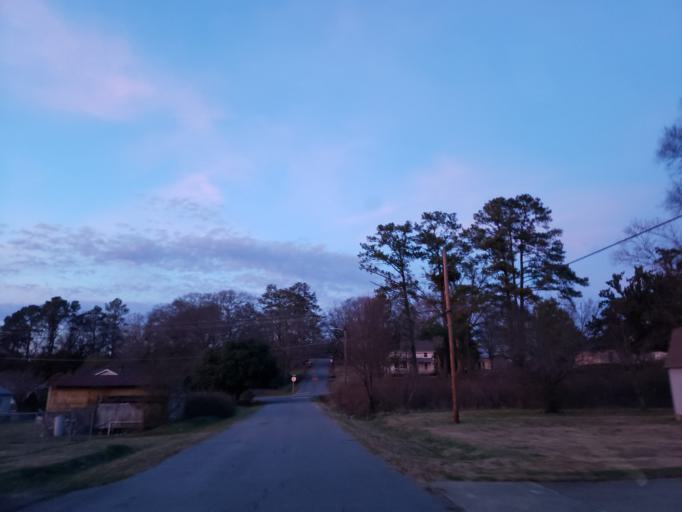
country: US
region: Georgia
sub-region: Bartow County
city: Emerson
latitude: 34.1264
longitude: -84.7543
